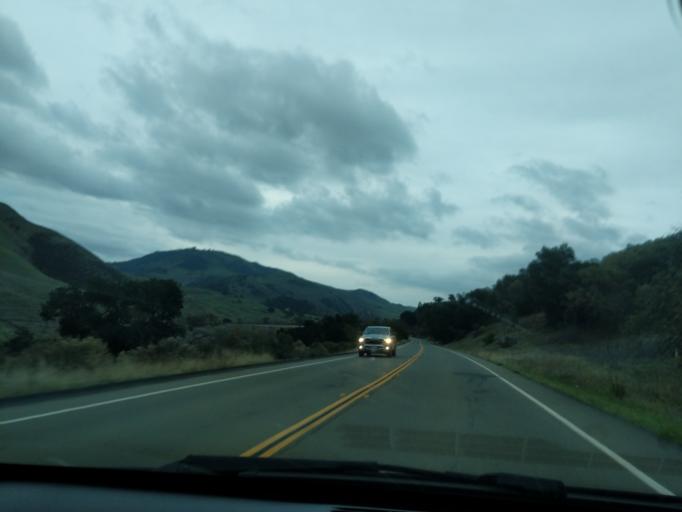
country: US
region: California
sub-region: Monterey County
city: Soledad
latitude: 36.6084
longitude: -121.2028
